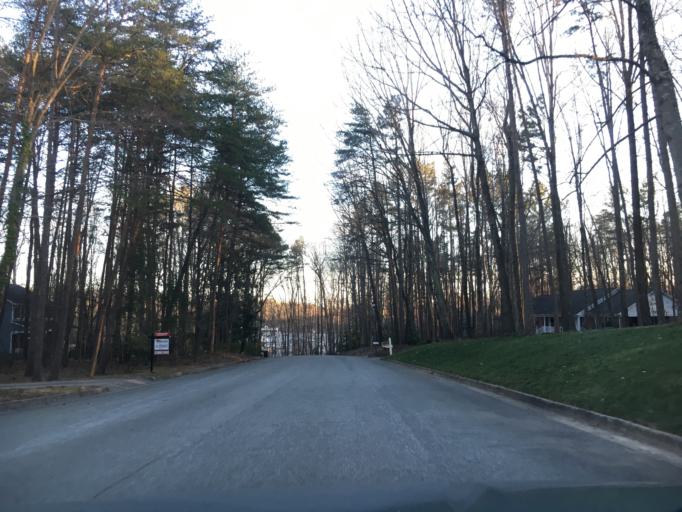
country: US
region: Virginia
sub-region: Halifax County
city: South Boston
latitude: 36.7172
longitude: -78.9137
